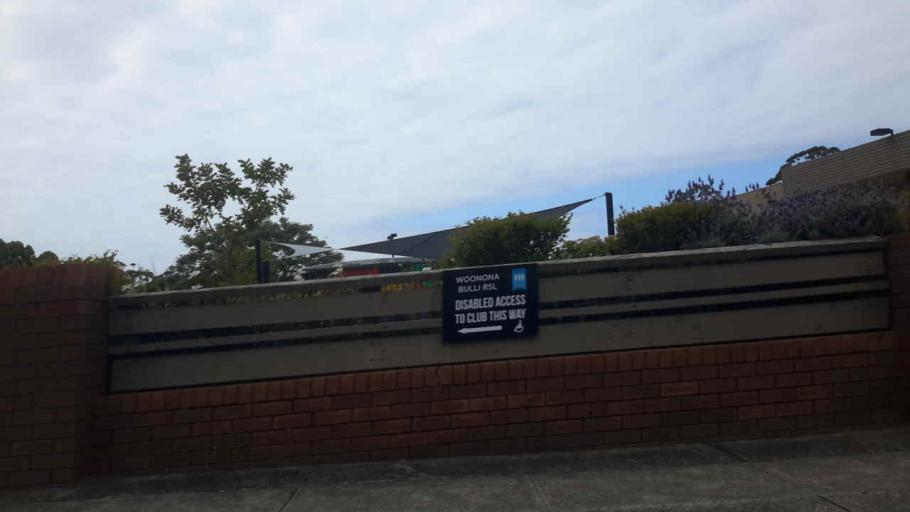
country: AU
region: New South Wales
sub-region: Wollongong
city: Bulli
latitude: -34.3433
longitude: 150.9045
